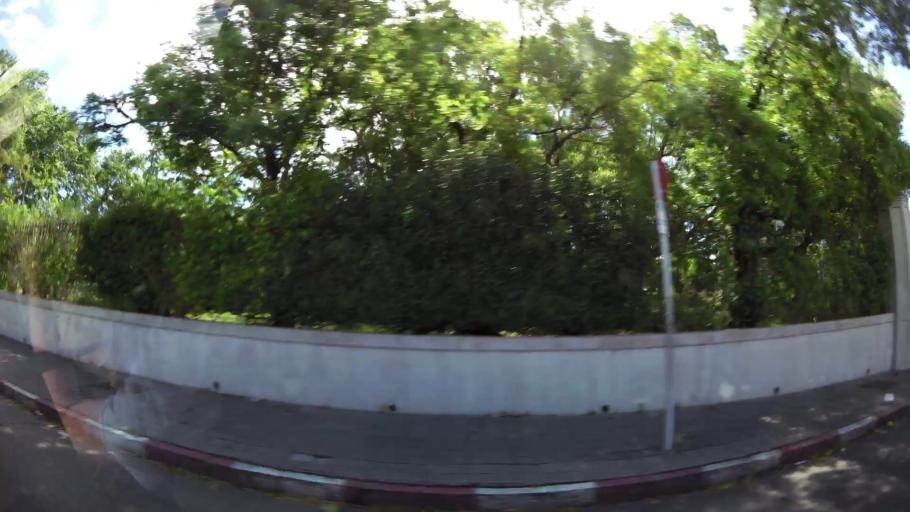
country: UY
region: Montevideo
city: Montevideo
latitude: -34.8607
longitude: -56.1966
